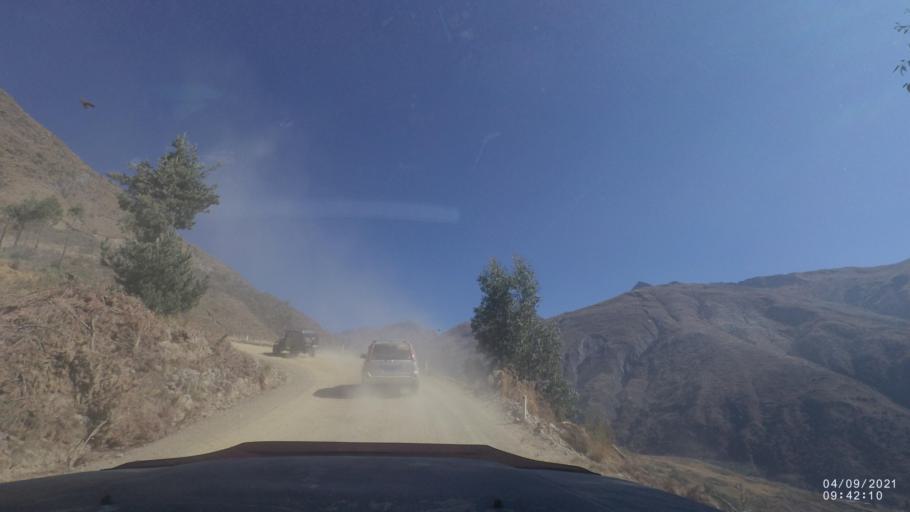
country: BO
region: Cochabamba
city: Sipe Sipe
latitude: -17.3394
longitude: -66.3891
